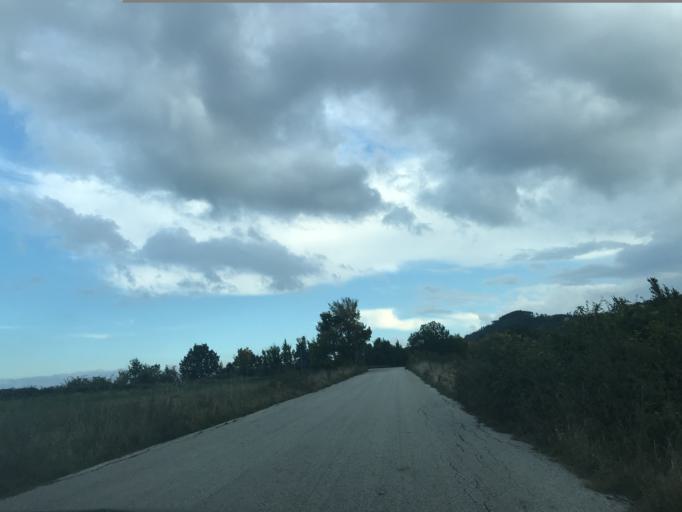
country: IT
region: Molise
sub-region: Provincia di Campobasso
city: Duronia
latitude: 41.6716
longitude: 14.4605
